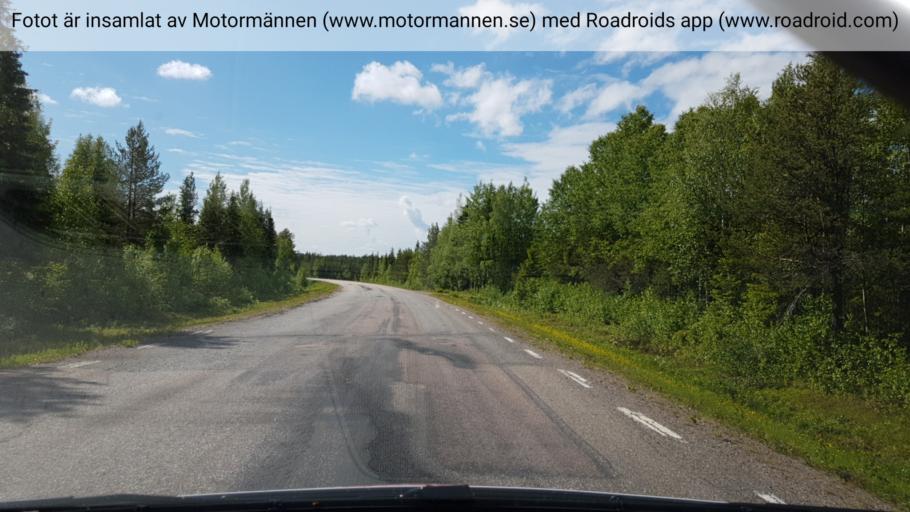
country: FI
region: Lapland
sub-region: Torniolaakso
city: Pello
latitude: 66.7631
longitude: 23.8679
